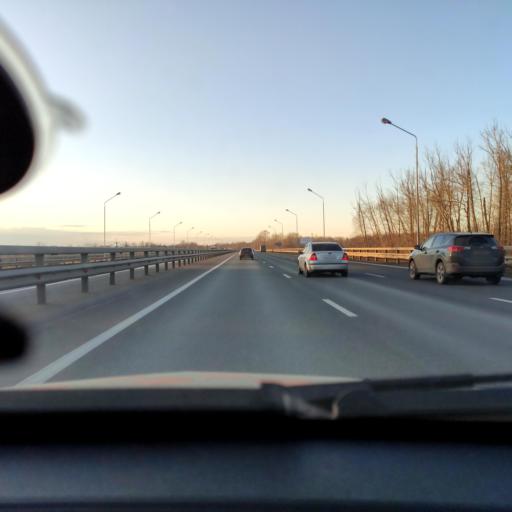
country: RU
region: Bashkortostan
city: Ufa
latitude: 54.6532
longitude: 55.8988
